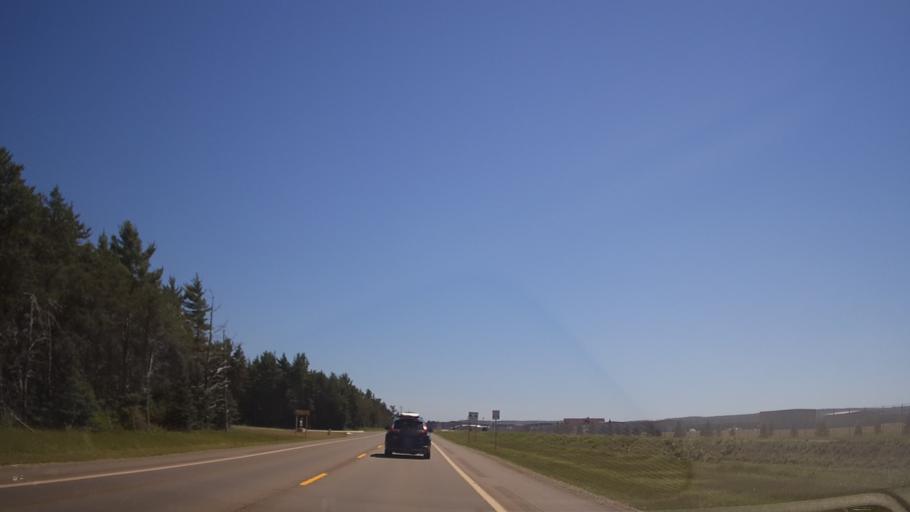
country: US
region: Michigan
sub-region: Cheboygan County
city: Indian River
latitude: 45.5788
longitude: -84.7834
